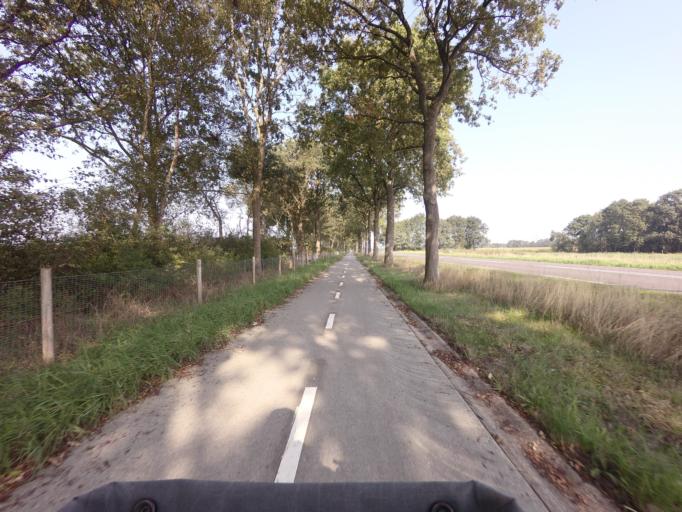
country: NL
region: Drenthe
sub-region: Gemeente Tynaarlo
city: Vries
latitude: 53.1144
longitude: 6.5143
